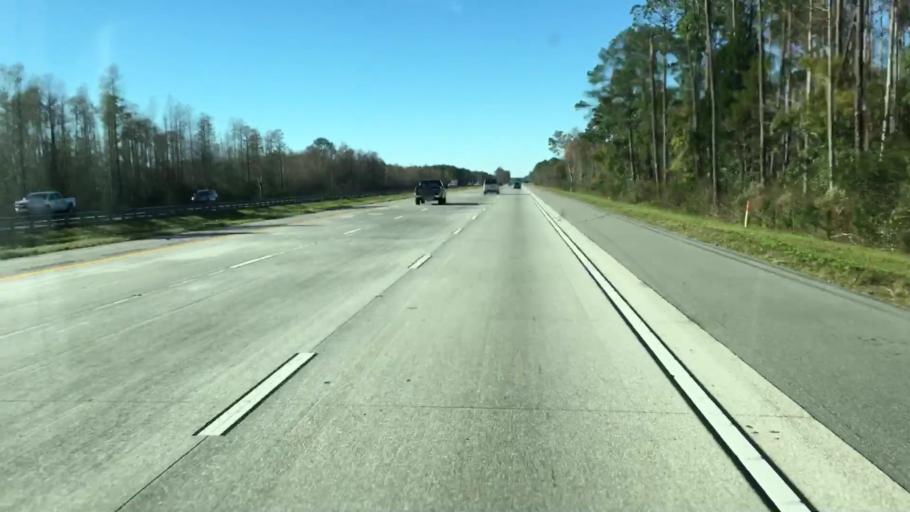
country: US
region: Florida
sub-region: Volusia County
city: Lake Helen
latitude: 29.0465
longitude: -81.2047
